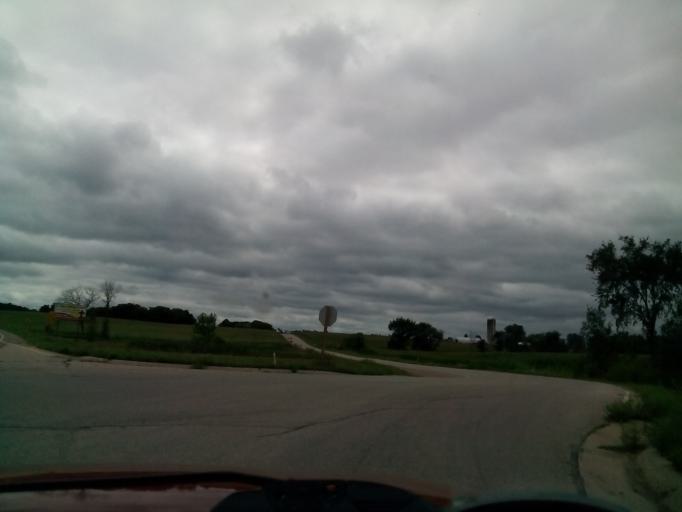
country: US
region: Wisconsin
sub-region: Oconto County
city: Gillett
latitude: 45.0049
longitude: -88.4171
